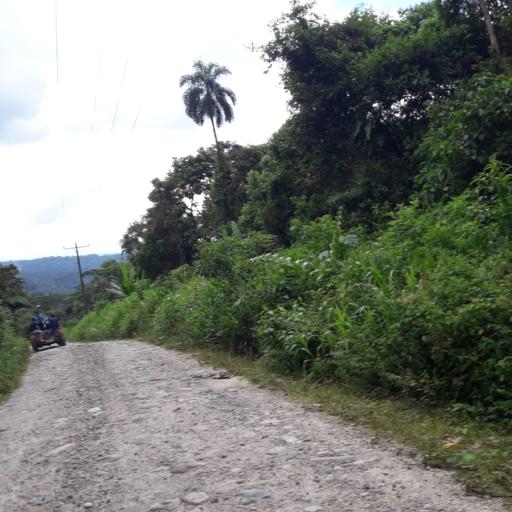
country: EC
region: Napo
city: Archidona
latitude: -0.9435
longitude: -77.8862
